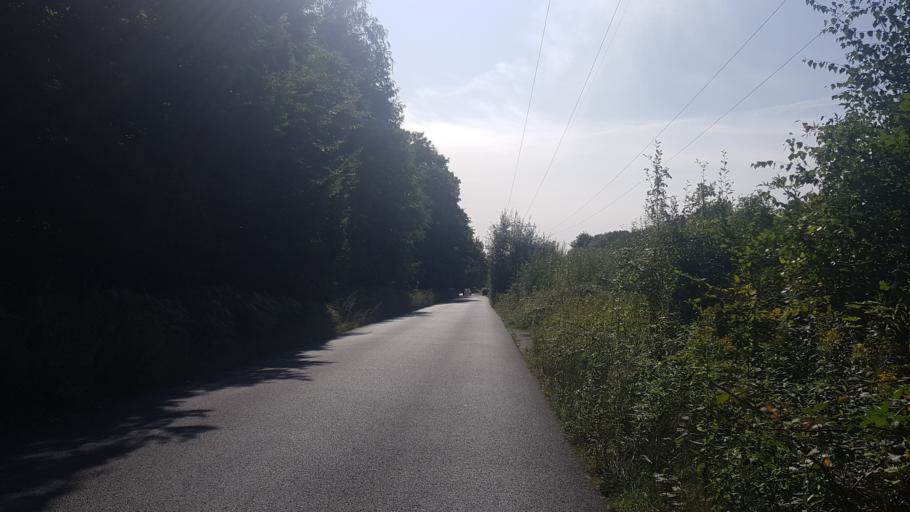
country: DE
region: North Rhine-Westphalia
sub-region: Regierungsbezirk Dusseldorf
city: Ratingen
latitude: 51.3573
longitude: 6.8188
